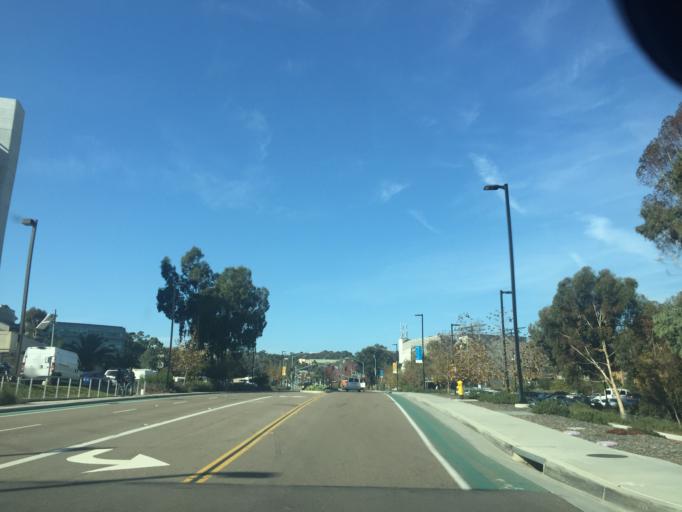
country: US
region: California
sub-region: San Diego County
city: La Jolla
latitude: 32.8765
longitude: -117.2314
